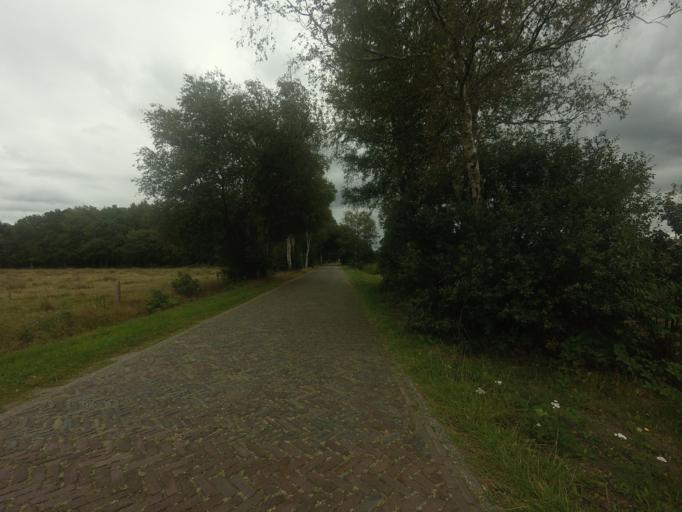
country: NL
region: Drenthe
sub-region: Gemeente Westerveld
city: Havelte
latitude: 52.8834
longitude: 6.2630
